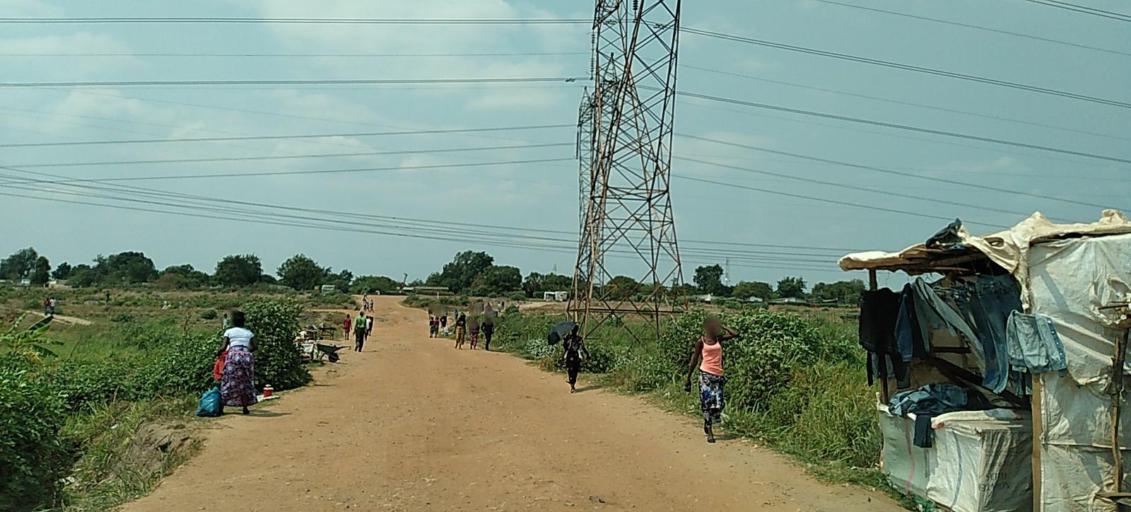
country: ZM
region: Copperbelt
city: Chambishi
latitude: -12.6333
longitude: 28.0698
